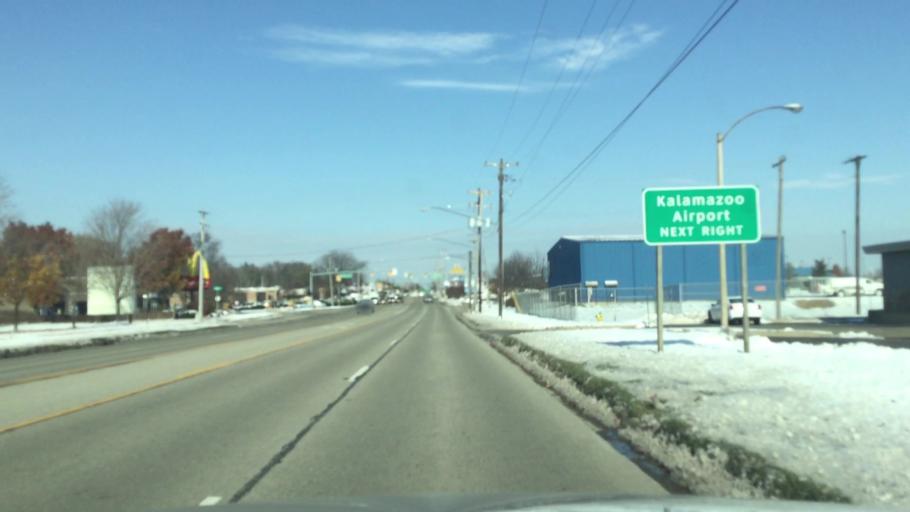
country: US
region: Michigan
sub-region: Kalamazoo County
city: Portage
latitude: 42.2366
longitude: -85.5601
